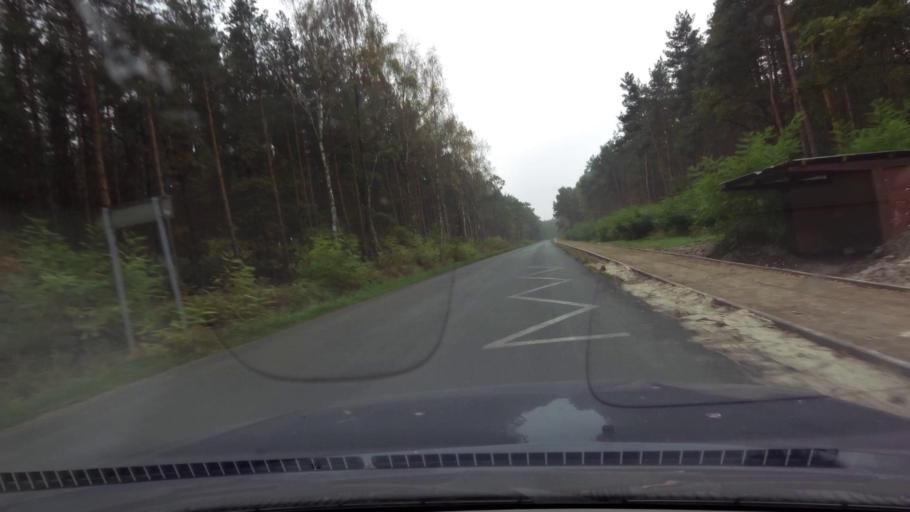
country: PL
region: West Pomeranian Voivodeship
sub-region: Powiat goleniowski
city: Goleniow
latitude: 53.5493
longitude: 14.7748
